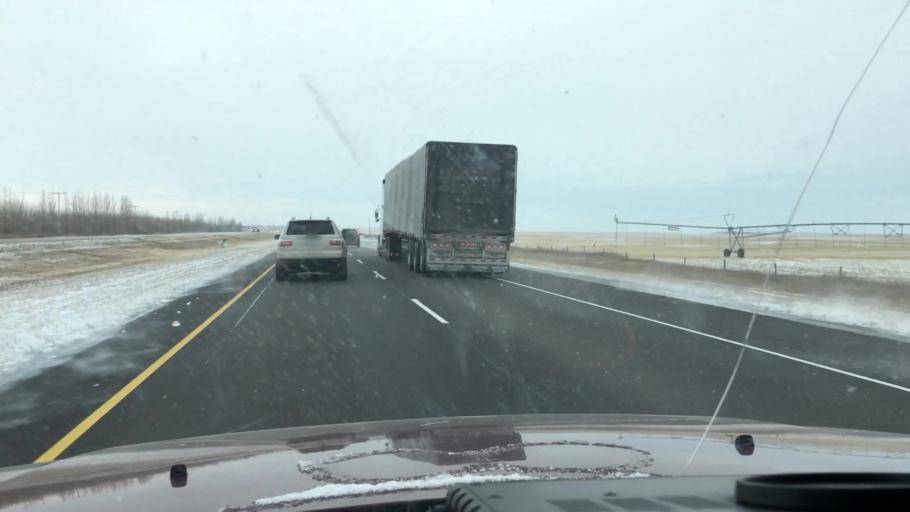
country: CA
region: Saskatchewan
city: Saskatoon
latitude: 51.7734
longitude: -106.4763
